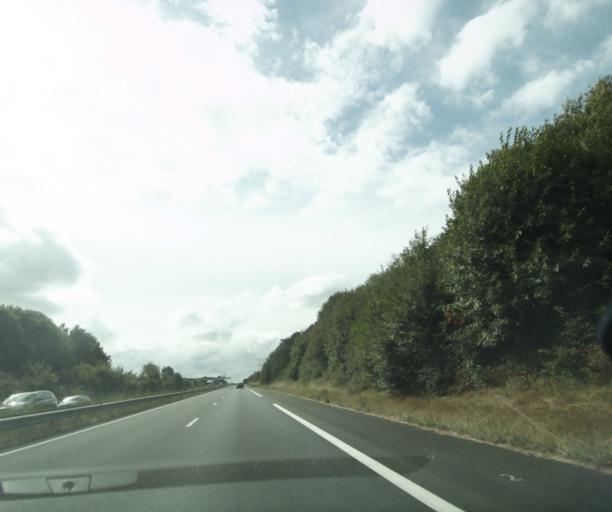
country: FR
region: Poitou-Charentes
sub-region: Departement de la Charente-Maritime
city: Pons
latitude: 45.5517
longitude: -0.6039
